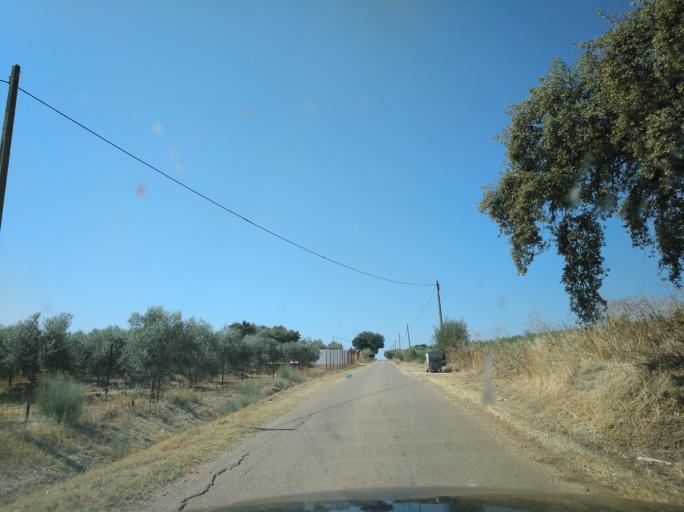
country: PT
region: Portalegre
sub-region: Campo Maior
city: Campo Maior
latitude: 39.0480
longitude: -7.0010
